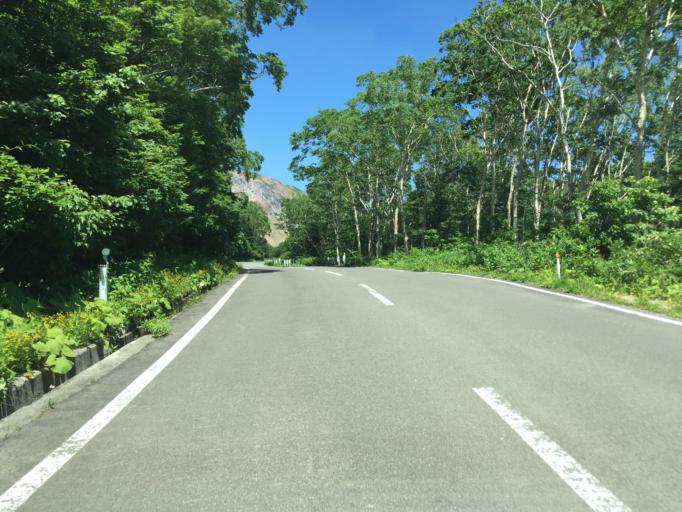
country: JP
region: Fukushima
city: Inawashiro
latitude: 37.7140
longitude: 140.2536
